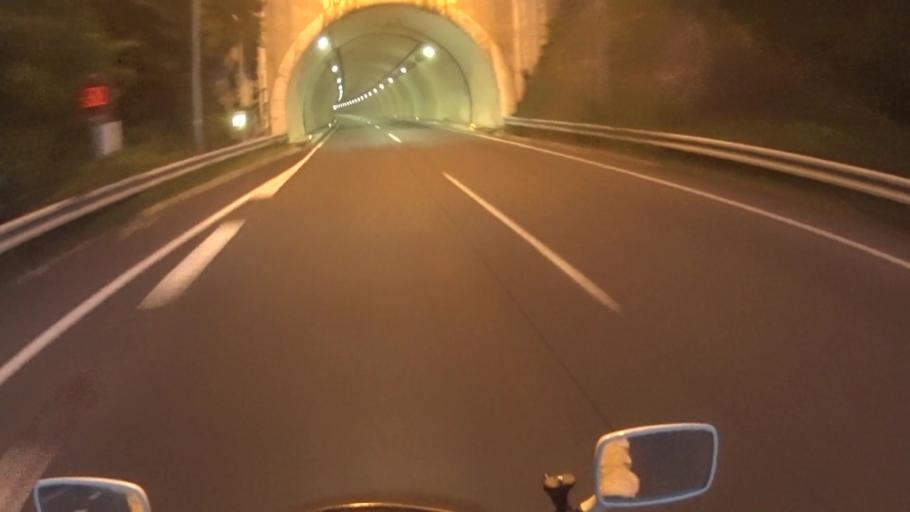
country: JP
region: Kyoto
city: Kameoka
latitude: 35.0711
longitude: 135.5196
